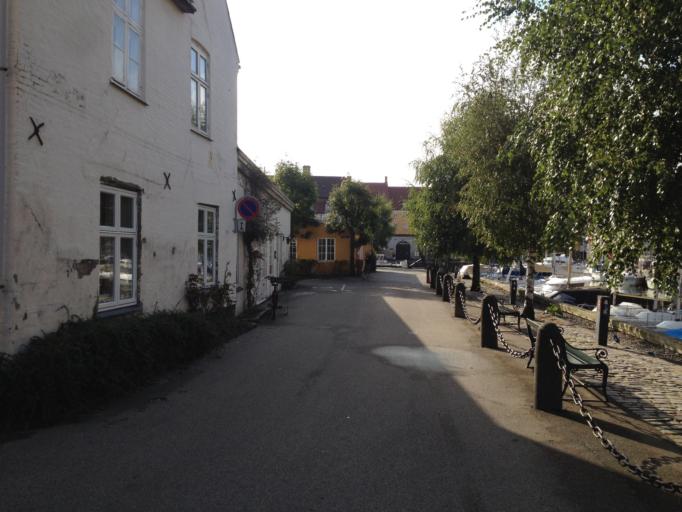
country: DK
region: Capital Region
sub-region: Kobenhavn
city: Christianshavn
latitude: 55.6754
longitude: 12.5934
